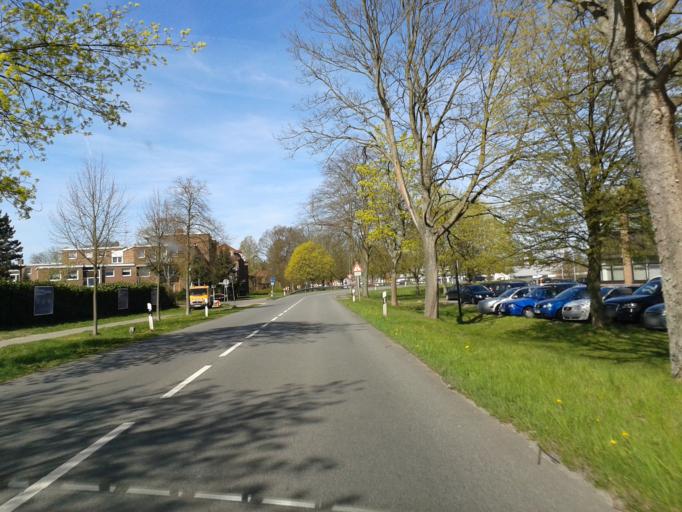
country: DE
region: Lower Saxony
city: Uelzen
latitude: 52.9626
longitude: 10.5811
